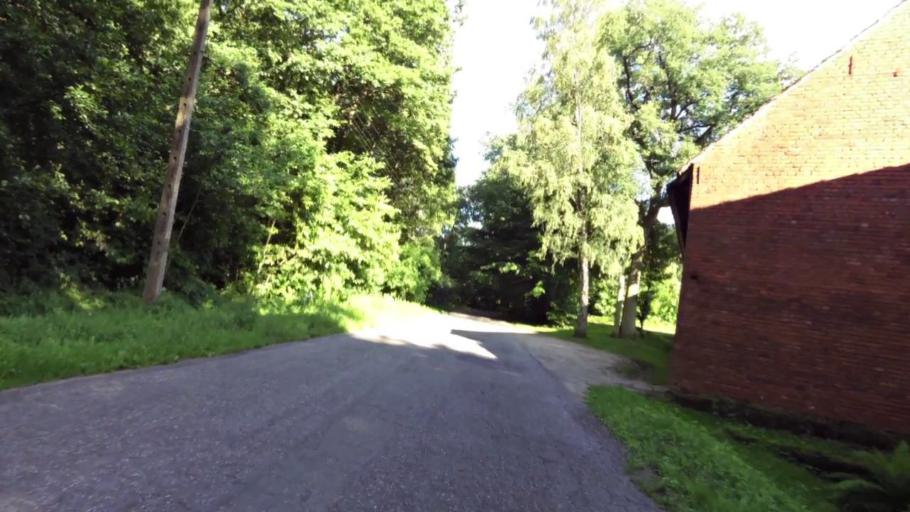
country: PL
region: West Pomeranian Voivodeship
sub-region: Powiat slawienski
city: Slawno
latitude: 54.4350
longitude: 16.7673
